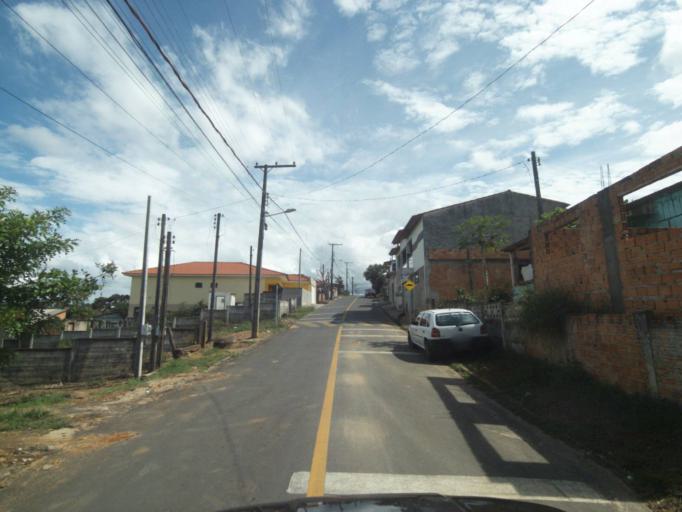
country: BR
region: Parana
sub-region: Telemaco Borba
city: Telemaco Borba
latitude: -24.3165
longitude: -50.6249
